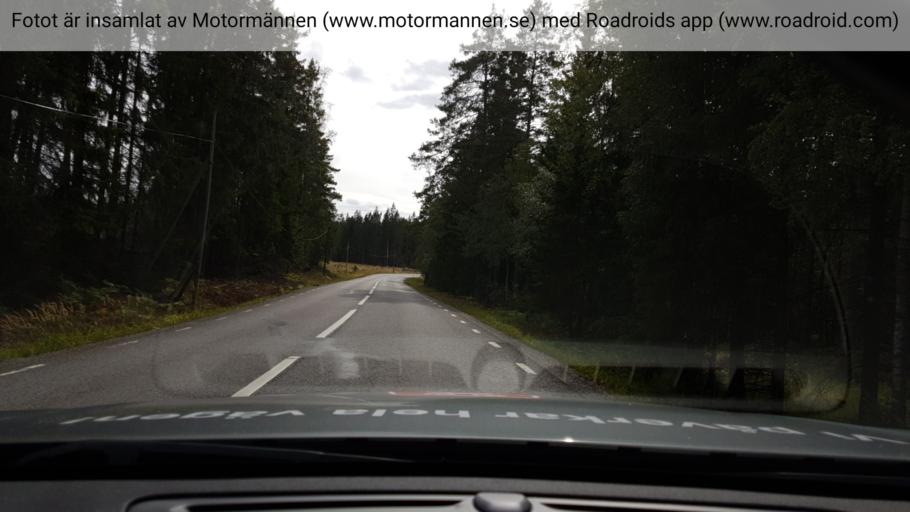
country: SE
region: Stockholm
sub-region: Botkyrka Kommun
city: Tullinge
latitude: 59.1316
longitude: 17.9364
